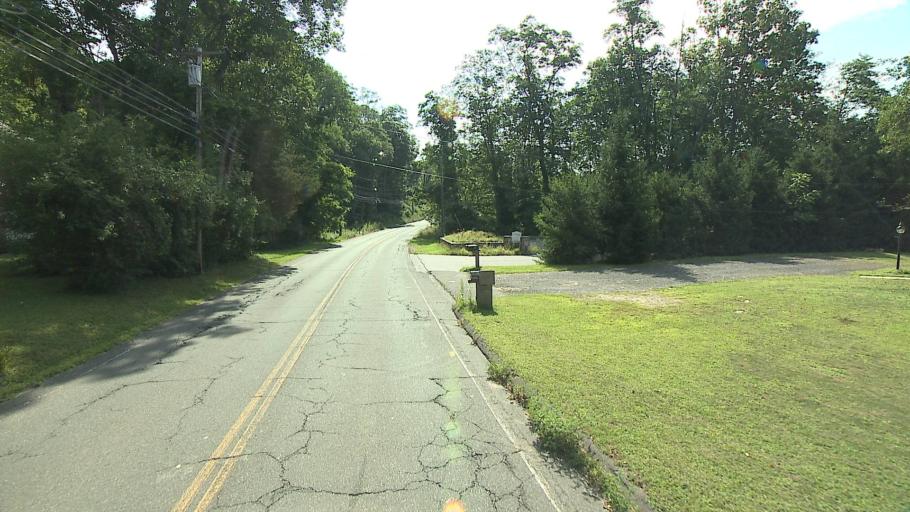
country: US
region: New York
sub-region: Putnam County
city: Putnam Lake
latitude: 41.4851
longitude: -73.5015
